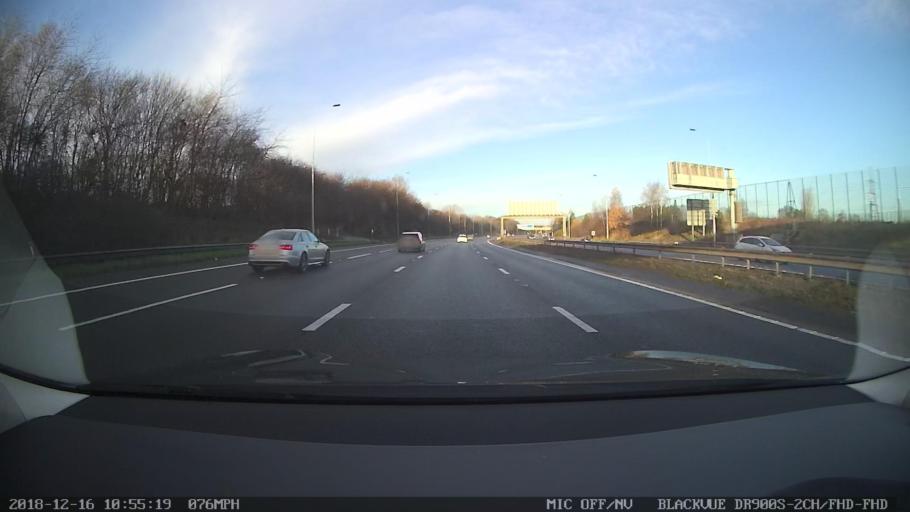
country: GB
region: England
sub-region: Manchester
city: Chorlton cum Hardy
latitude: 53.4168
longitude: -2.2844
